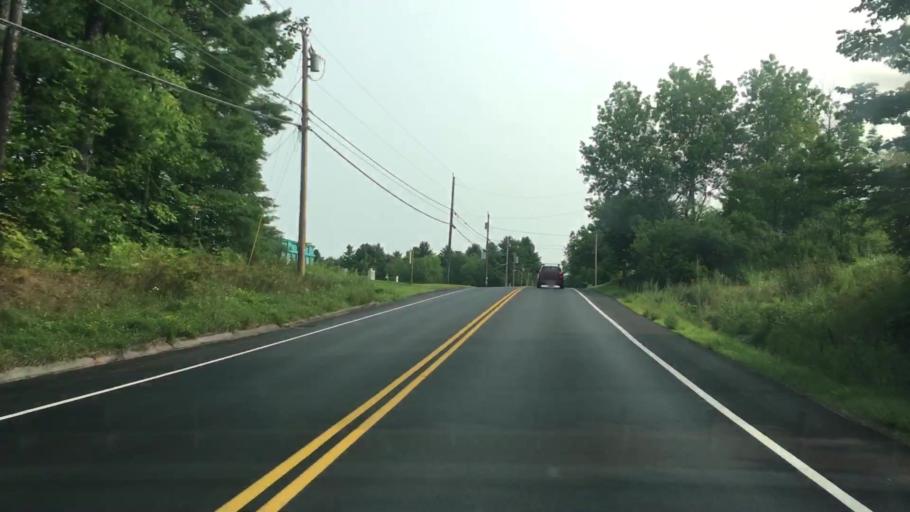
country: US
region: Maine
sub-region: Kennebec County
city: Chelsea
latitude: 44.2668
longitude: -69.6997
